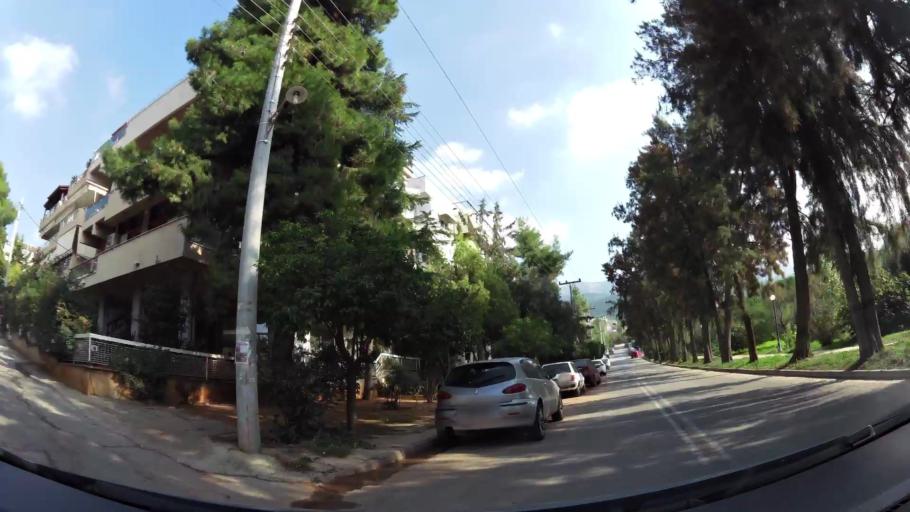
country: GR
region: Attica
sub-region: Nomos Attikis
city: Zografos
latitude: 37.9794
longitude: 23.7899
